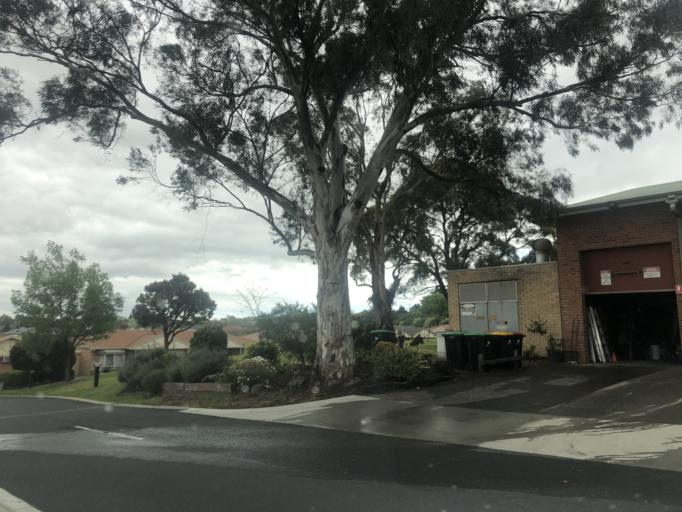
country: AU
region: Victoria
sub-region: Greater Dandenong
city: Dandenong North
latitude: -37.9769
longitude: 145.2260
